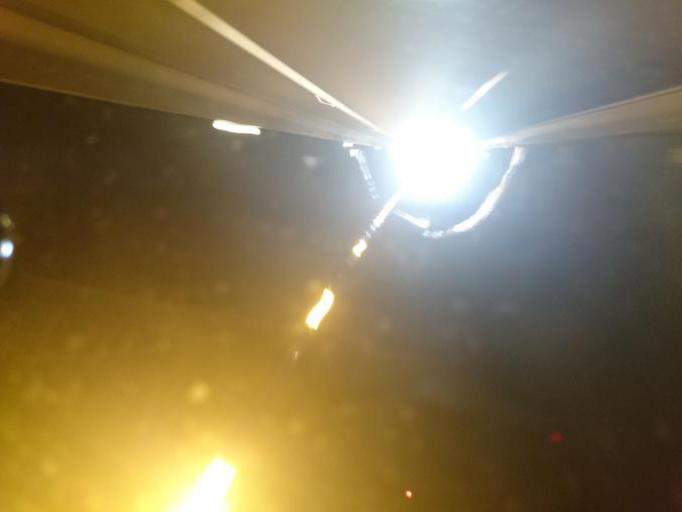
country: ES
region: Catalonia
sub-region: Provincia de Barcelona
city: Castelldefels
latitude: 41.2604
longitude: 1.9162
